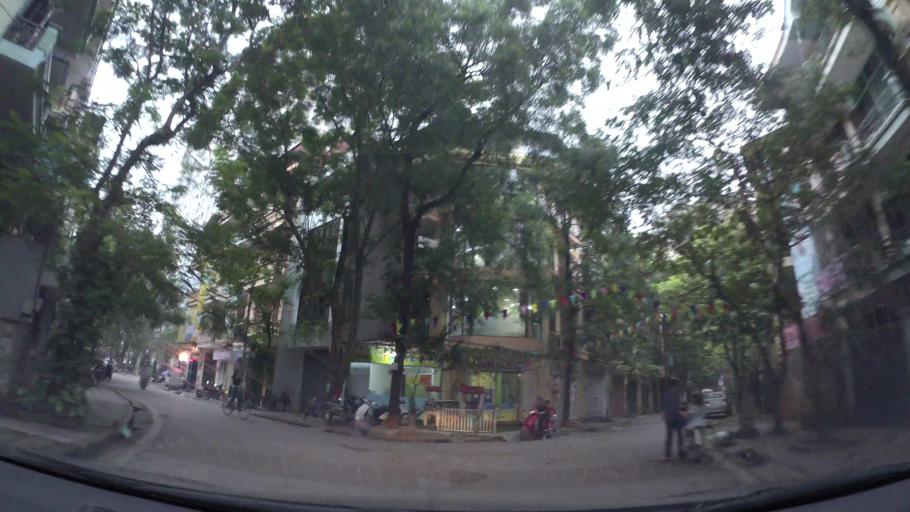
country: VN
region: Ha Noi
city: Hai BaTrung
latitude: 20.9854
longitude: 105.8322
